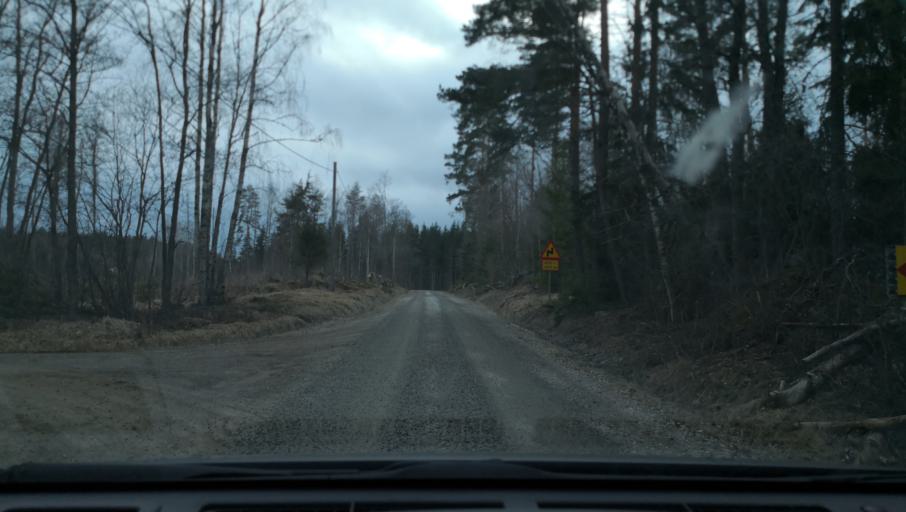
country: SE
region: Vaestmanland
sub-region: Kopings Kommun
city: Kolsva
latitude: 59.6007
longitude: 15.6809
